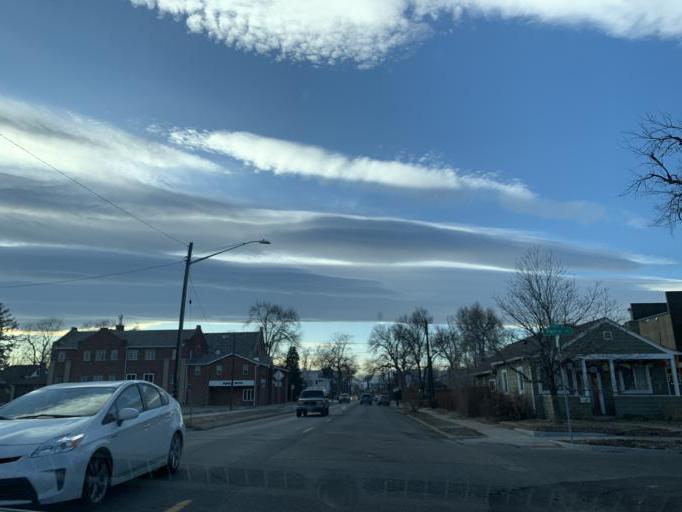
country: US
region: Colorado
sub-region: Adams County
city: Berkley
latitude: 39.7767
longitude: -105.0391
